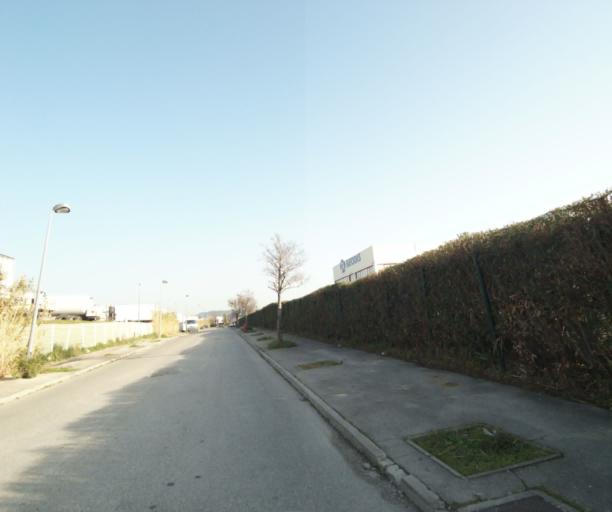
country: FR
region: Provence-Alpes-Cote d'Azur
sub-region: Departement des Bouches-du-Rhone
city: Saint-Victoret
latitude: 43.4241
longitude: 5.2631
